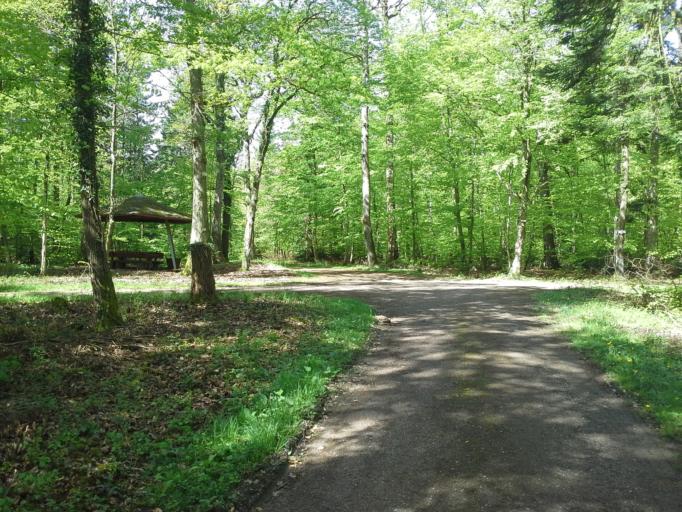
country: DE
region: Baden-Wuerttemberg
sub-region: Karlsruhe Region
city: Ispringen
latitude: 48.9050
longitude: 8.6370
